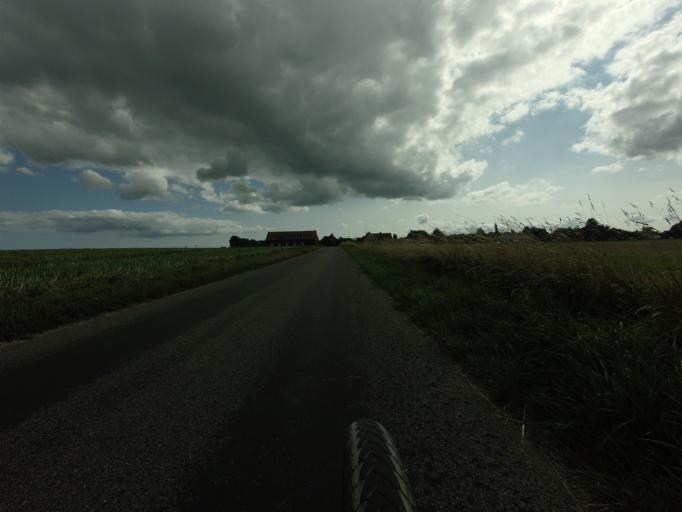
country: DK
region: Zealand
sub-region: Vordingborg Kommune
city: Stege
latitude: 55.0055
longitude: 12.3170
